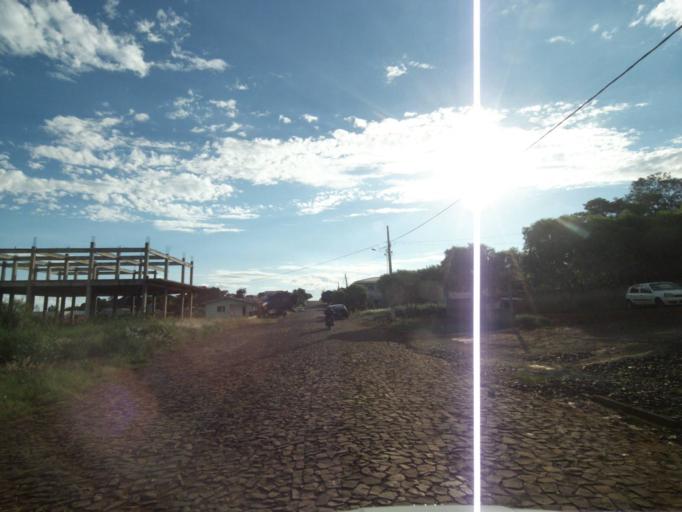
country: BR
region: Parana
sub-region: Laranjeiras Do Sul
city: Laranjeiras do Sul
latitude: -25.4937
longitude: -52.5299
